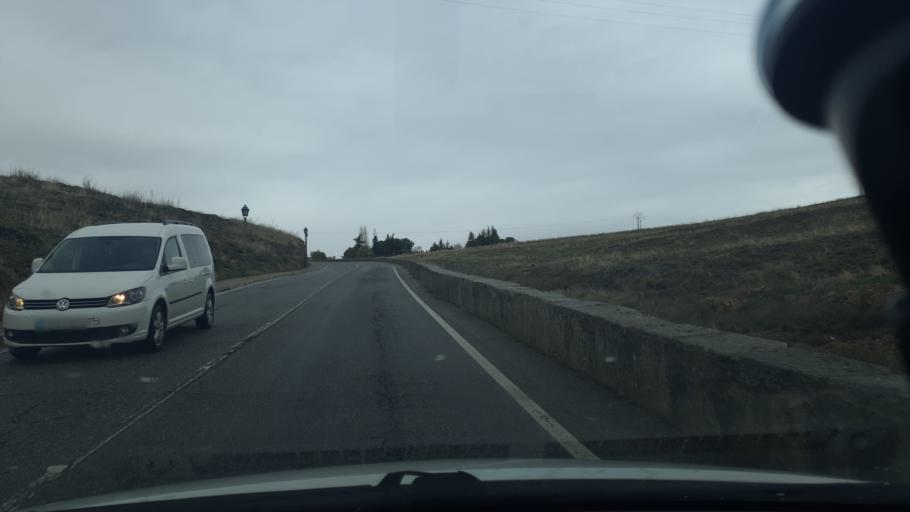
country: ES
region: Castille and Leon
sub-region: Provincia de Segovia
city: Segovia
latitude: 40.9597
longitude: -4.1334
